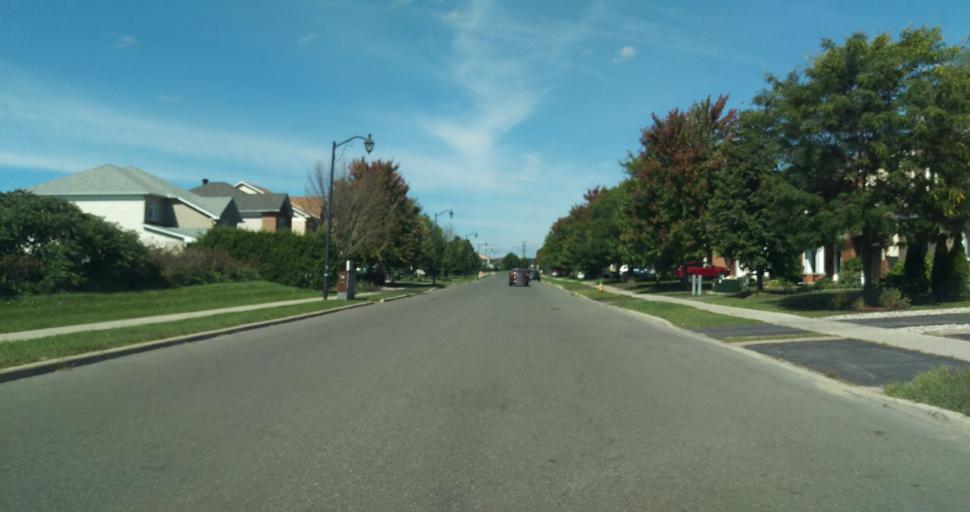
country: CA
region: Ontario
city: Clarence-Rockland
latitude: 45.4551
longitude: -75.4738
